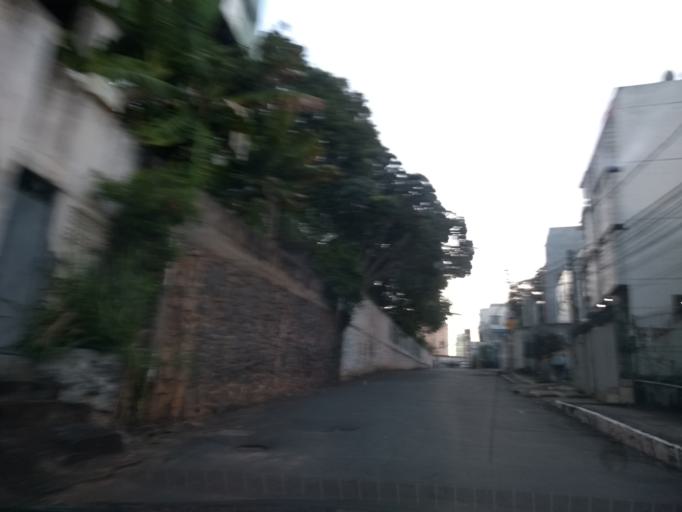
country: BR
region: Bahia
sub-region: Salvador
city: Salvador
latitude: -13.0067
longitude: -38.4855
